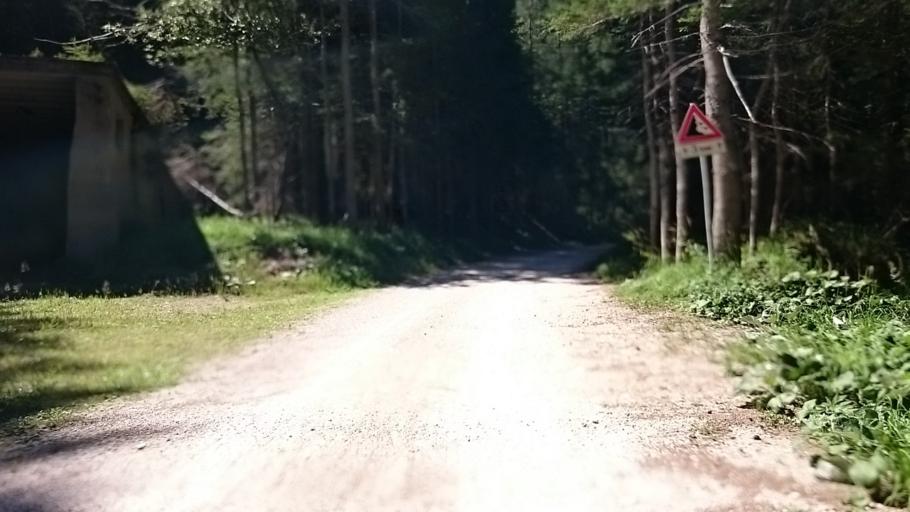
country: IT
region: Veneto
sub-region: Provincia di Belluno
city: Cortina d'Ampezzo
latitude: 46.5968
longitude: 12.1182
